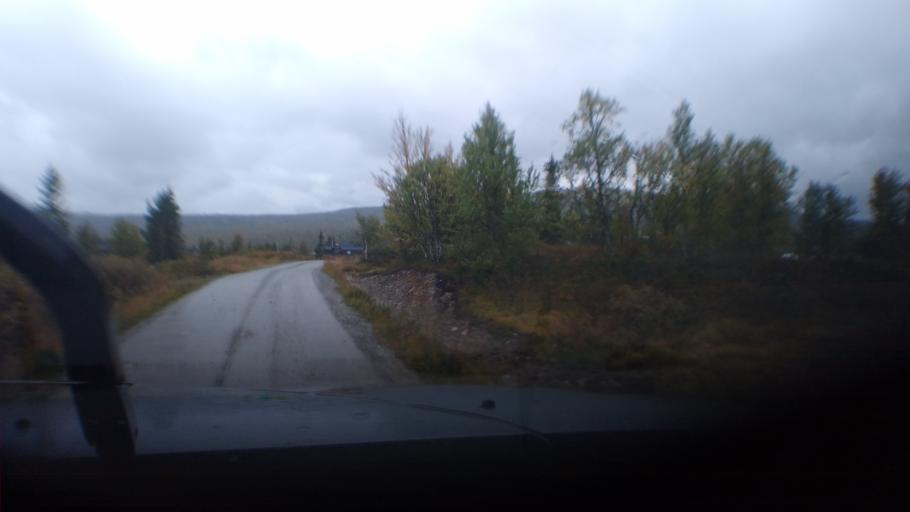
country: NO
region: Oppland
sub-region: Ringebu
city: Ringebu
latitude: 61.6505
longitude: 10.0959
